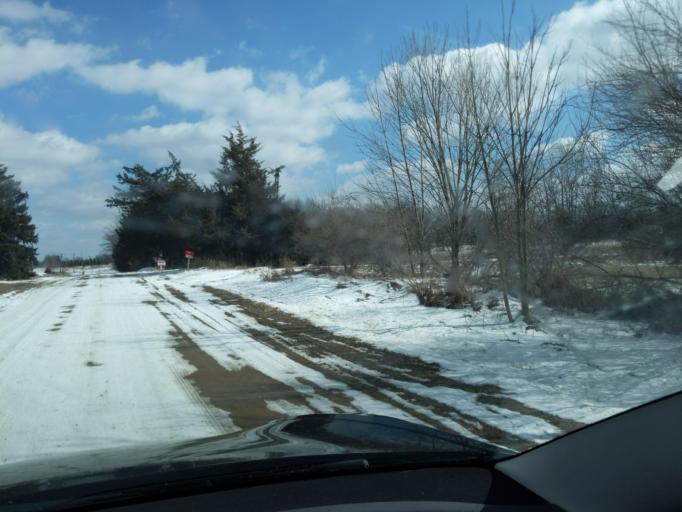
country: US
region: Michigan
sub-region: Livingston County
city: Fowlerville
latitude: 42.6139
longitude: -84.0645
